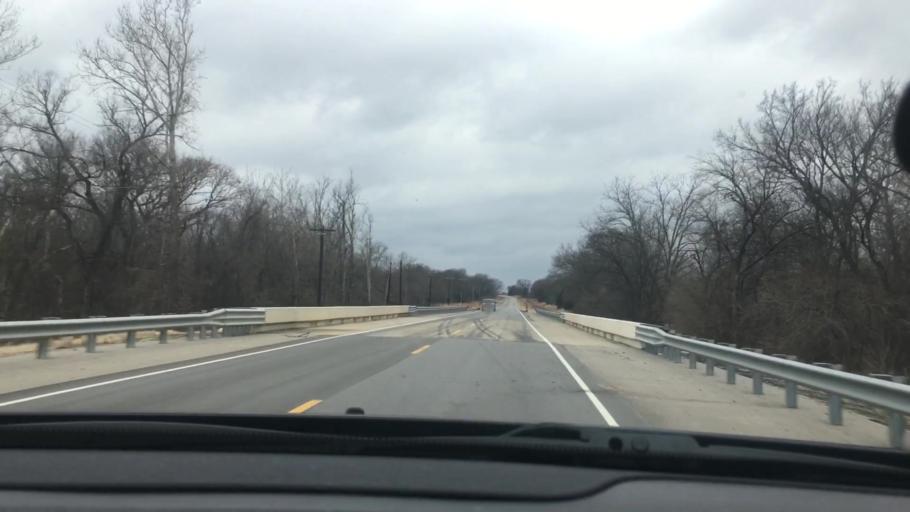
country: US
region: Oklahoma
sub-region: Atoka County
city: Atoka
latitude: 34.3791
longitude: -96.2786
